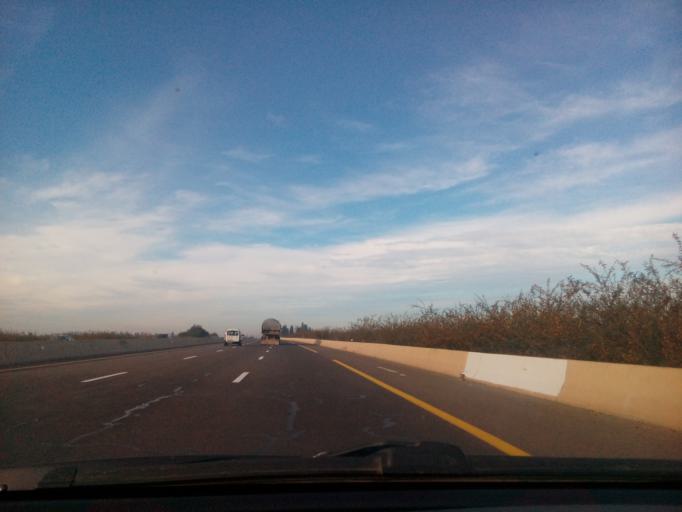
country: DZ
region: Mascara
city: Sig
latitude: 35.6159
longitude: 0.0001
